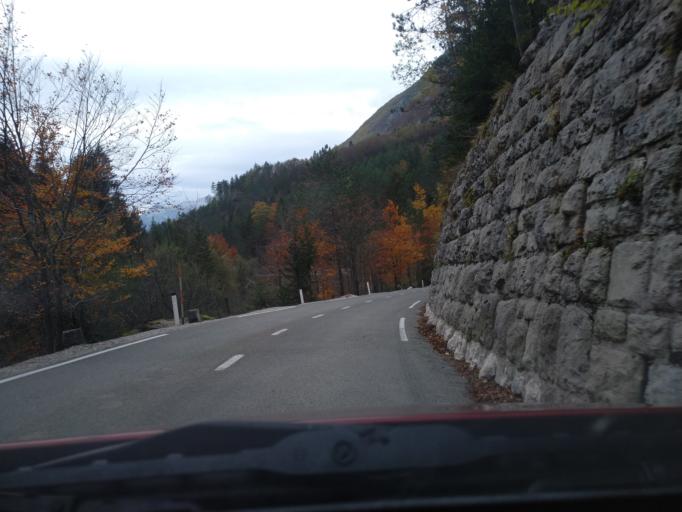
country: SI
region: Bovec
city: Bovec
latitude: 46.3376
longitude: 13.6200
